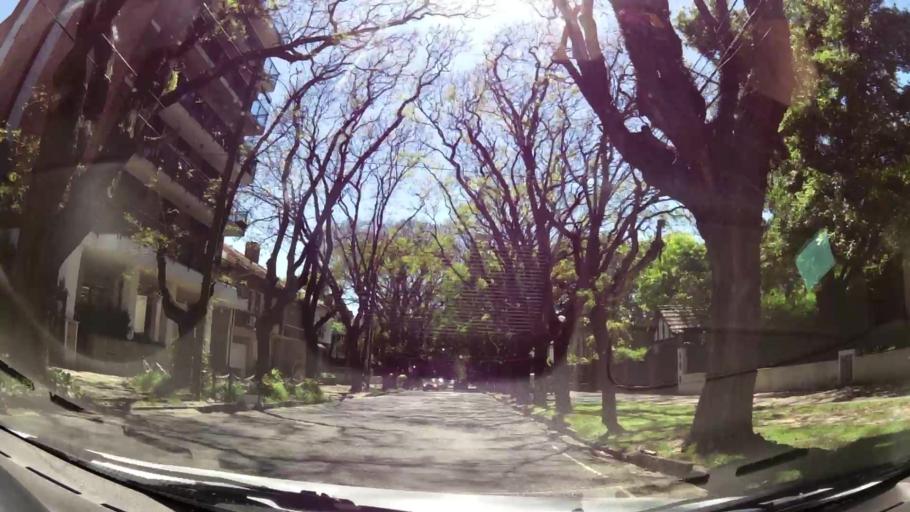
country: AR
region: Buenos Aires
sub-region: Partido de Vicente Lopez
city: Olivos
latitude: -34.5114
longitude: -58.4857
